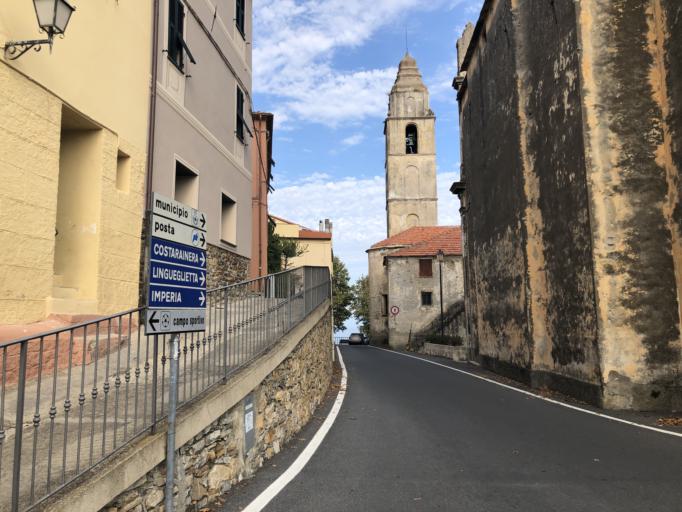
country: IT
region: Liguria
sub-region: Provincia di Imperia
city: Cipressa
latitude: 43.8516
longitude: 7.9309
